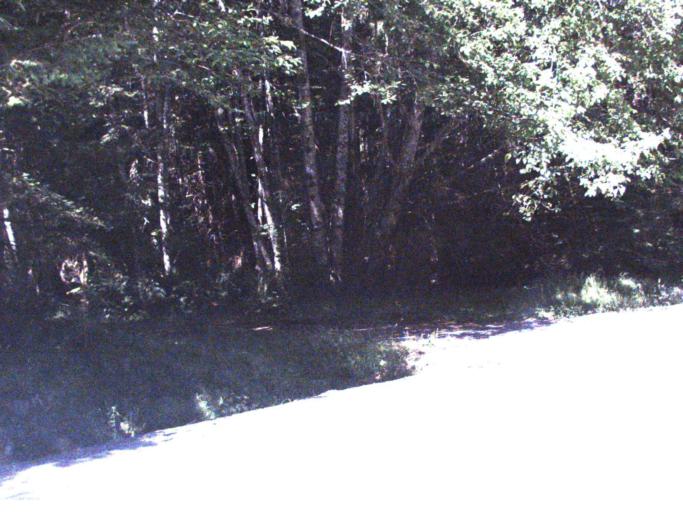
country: US
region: Washington
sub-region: King County
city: Riverbend
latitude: 47.1492
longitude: -121.6441
